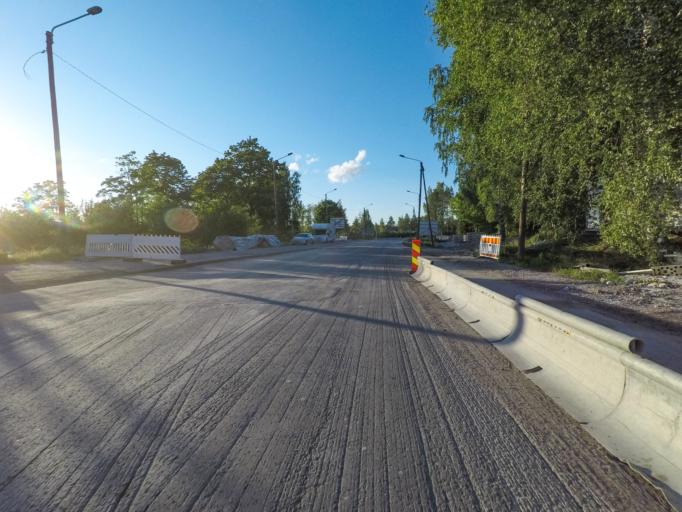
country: FI
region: South Karelia
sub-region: Imatra
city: Imatra
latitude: 61.1976
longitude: 28.7837
